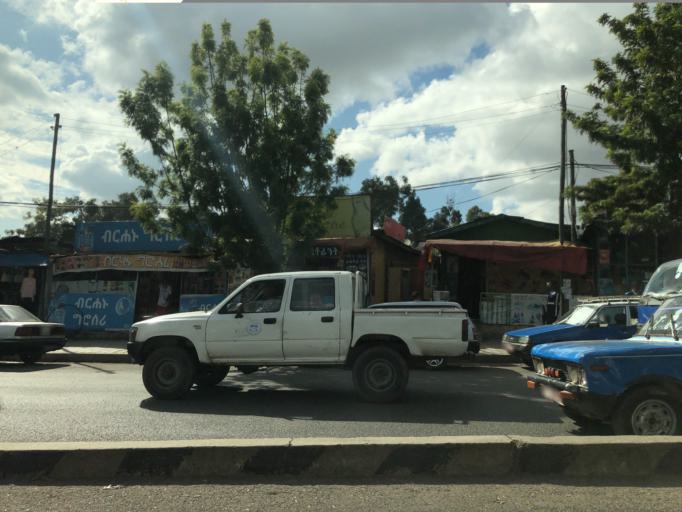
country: ET
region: Adis Abeba
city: Addis Ababa
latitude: 9.0238
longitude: 38.7766
